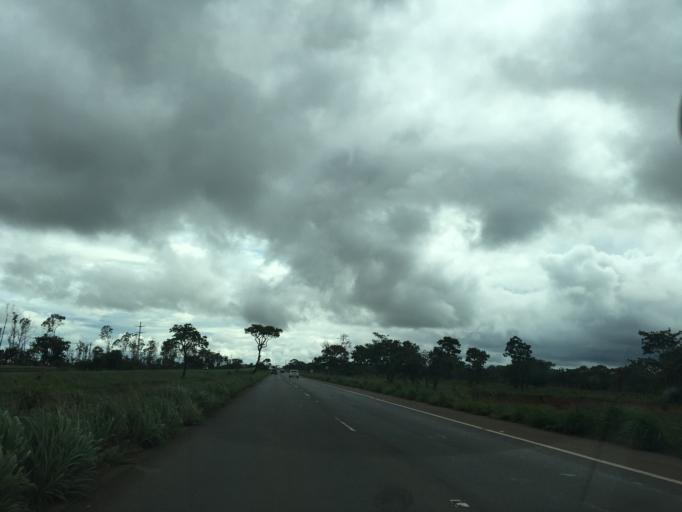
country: BR
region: Federal District
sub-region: Brasilia
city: Brasilia
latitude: -15.9171
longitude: -47.8263
